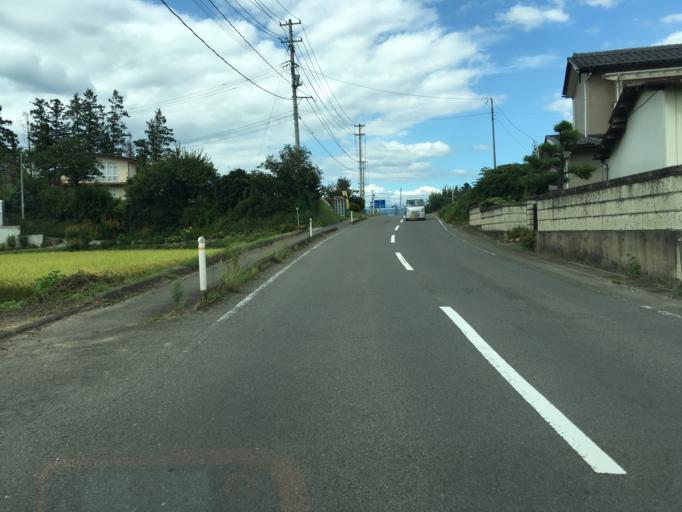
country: JP
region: Fukushima
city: Fukushima-shi
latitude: 37.7562
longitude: 140.4193
